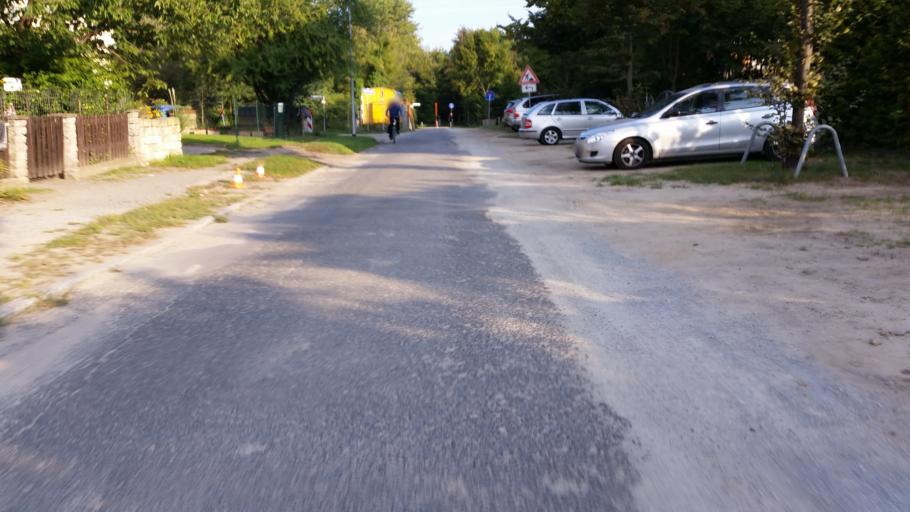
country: DE
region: Berlin
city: Lichterfelde
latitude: 52.4133
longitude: 13.2963
